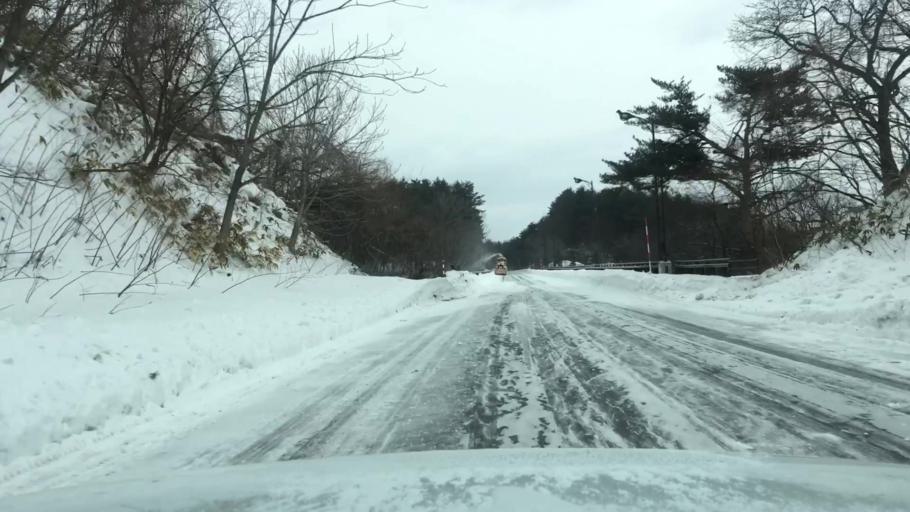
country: JP
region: Iwate
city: Shizukuishi
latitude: 39.9445
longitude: 140.9968
